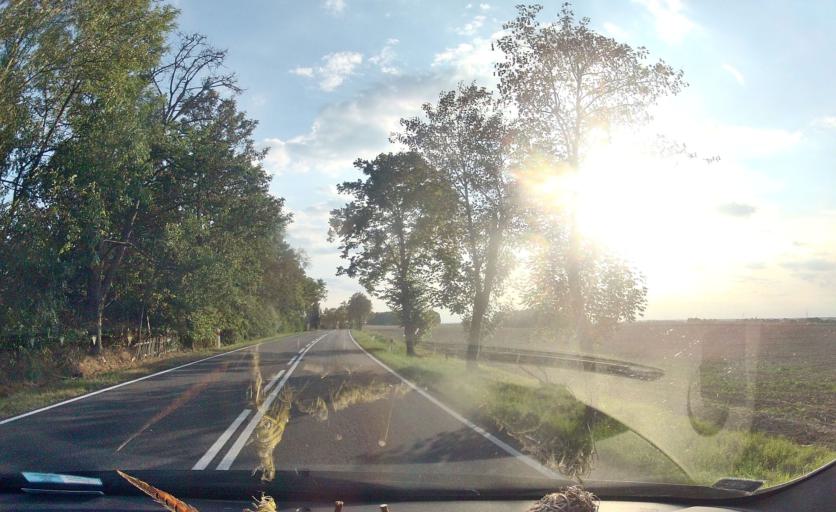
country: PL
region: Opole Voivodeship
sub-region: Powiat kluczborski
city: Kluczbork
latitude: 50.9948
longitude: 18.2994
